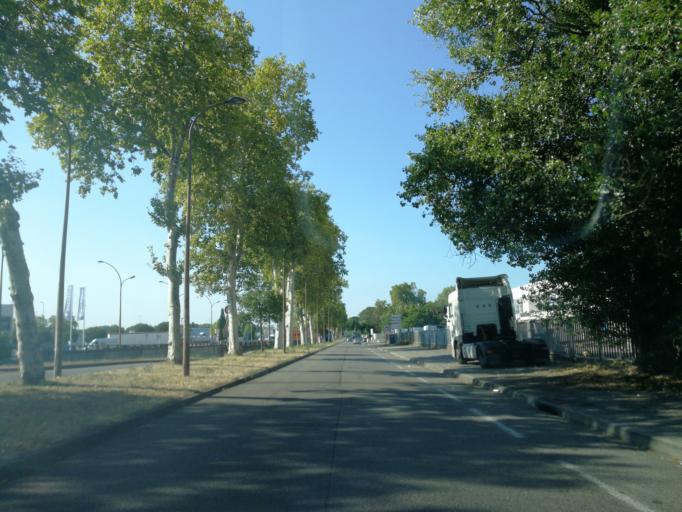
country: FR
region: Midi-Pyrenees
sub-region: Departement de la Haute-Garonne
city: Aucamville
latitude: 43.6411
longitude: 1.4289
